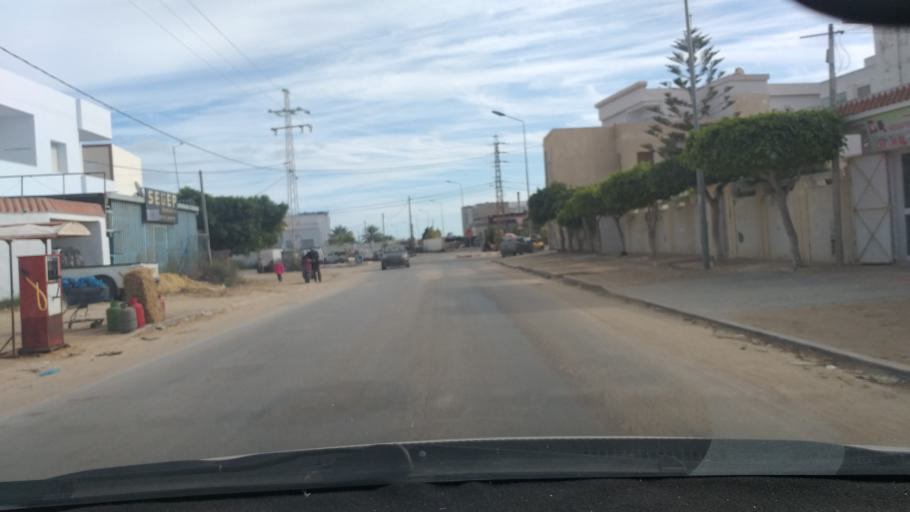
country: TN
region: Safaqis
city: Al Qarmadah
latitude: 34.7918
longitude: 10.8050
